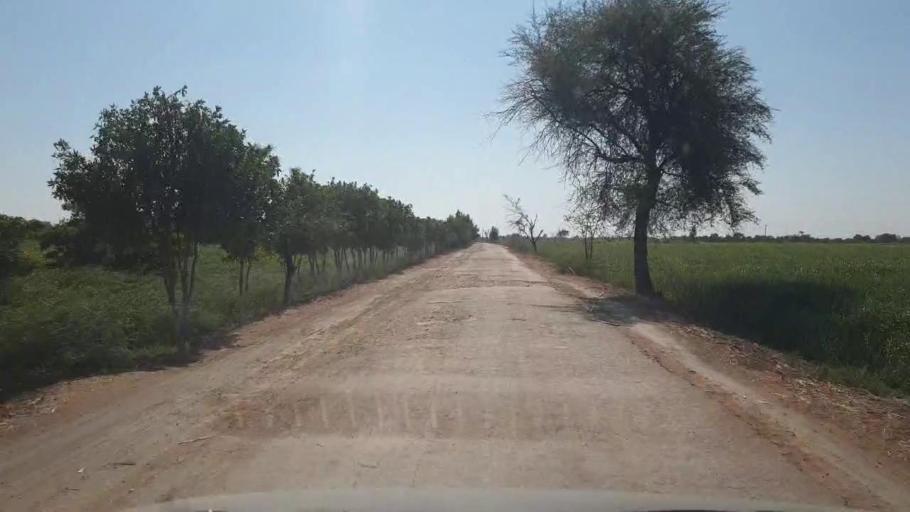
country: PK
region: Sindh
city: Mirwah Gorchani
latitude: 25.3083
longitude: 69.1294
